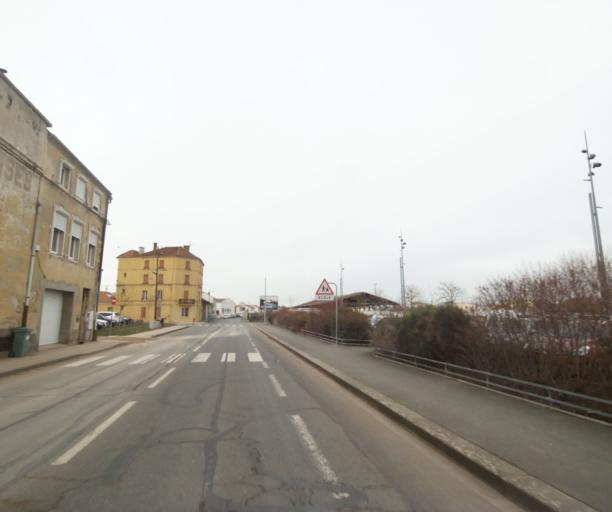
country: FR
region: Rhone-Alpes
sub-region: Departement de la Loire
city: Roanne
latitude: 46.0403
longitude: 4.0611
